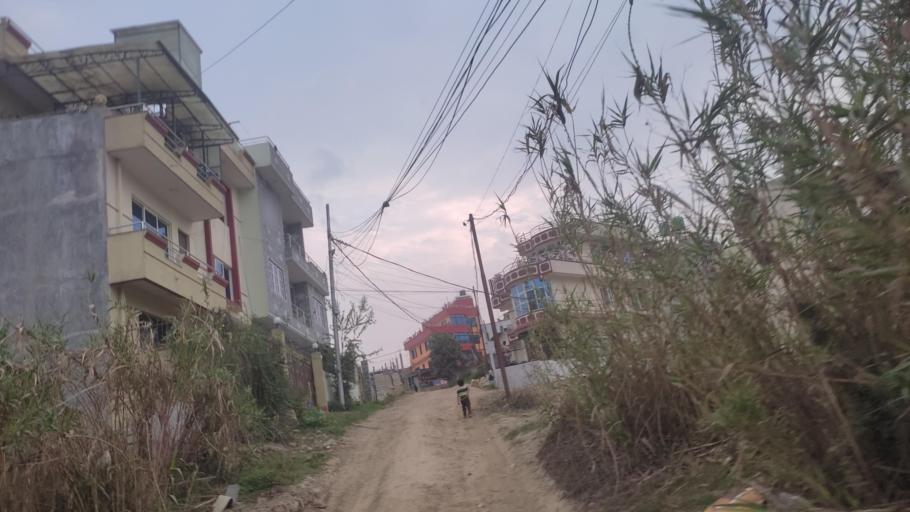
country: NP
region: Central Region
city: Kirtipur
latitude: 27.6607
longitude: 85.2874
